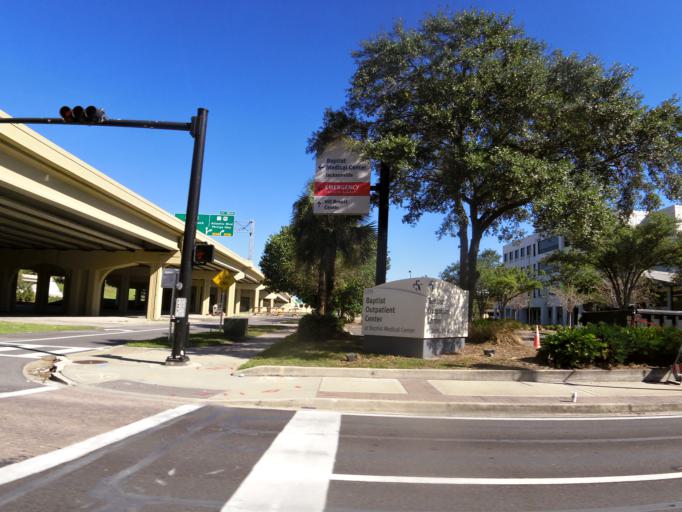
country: US
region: Florida
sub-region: Duval County
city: Jacksonville
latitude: 30.3135
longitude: -81.6605
